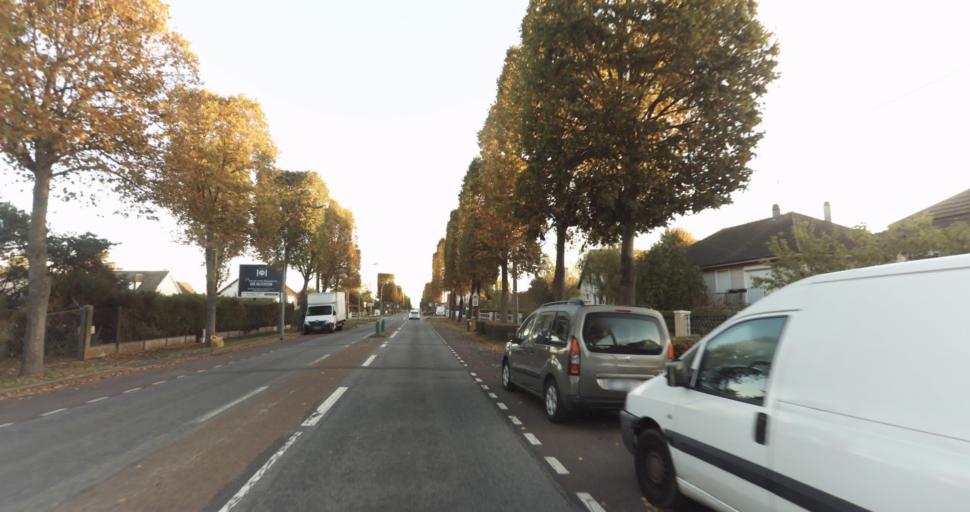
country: FR
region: Centre
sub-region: Departement d'Eure-et-Loir
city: Vernouillet
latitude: 48.7138
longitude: 1.3615
